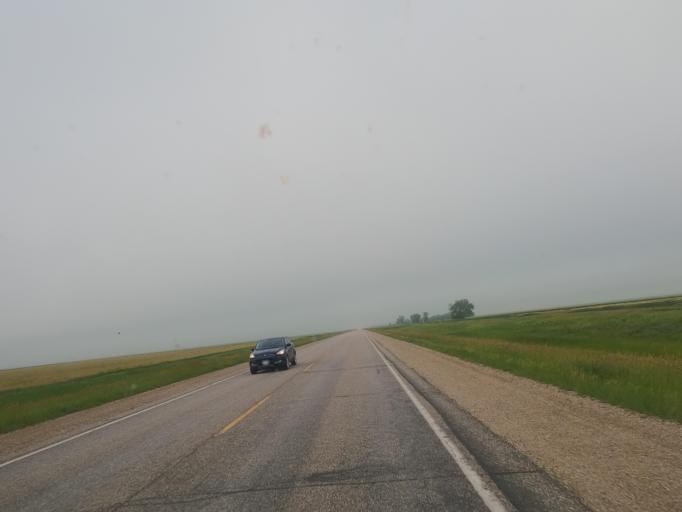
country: CA
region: Manitoba
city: Carman
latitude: 49.7285
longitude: -97.8655
